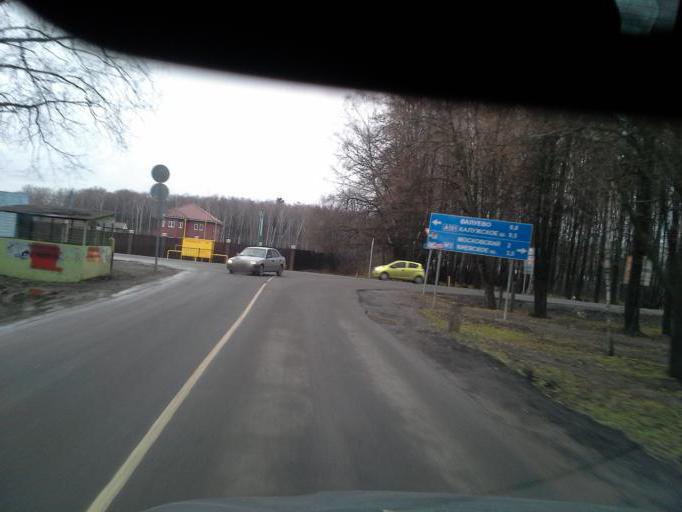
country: RU
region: Moskovskaya
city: Moskovskiy
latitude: 55.5820
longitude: 37.3605
